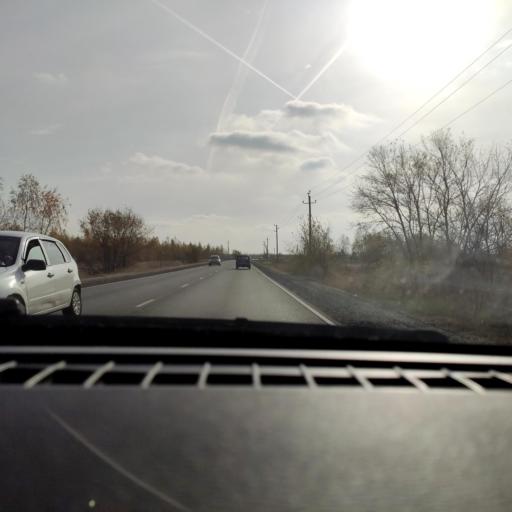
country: RU
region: Voronezj
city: Maslovka
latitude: 51.5801
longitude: 39.2631
